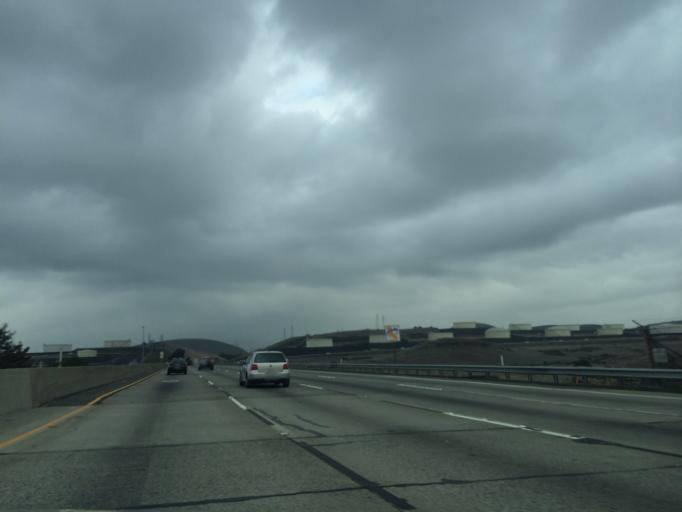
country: US
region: California
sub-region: Contra Costa County
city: Rodeo
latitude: 38.0340
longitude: -122.2518
